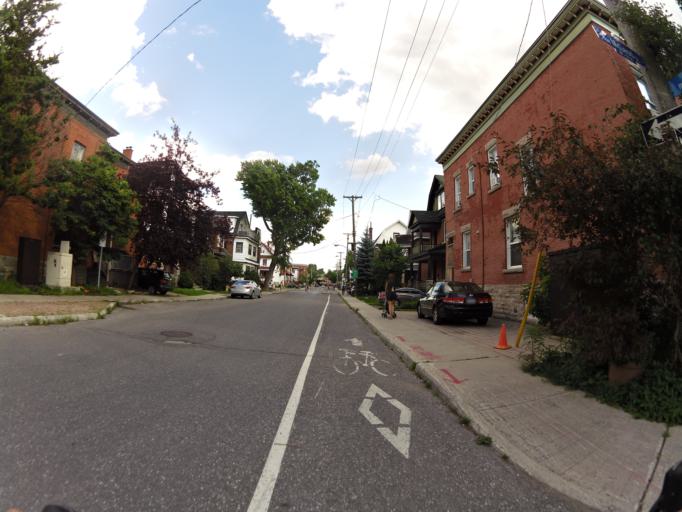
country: CA
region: Ontario
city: Ottawa
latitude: 45.4084
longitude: -75.7007
